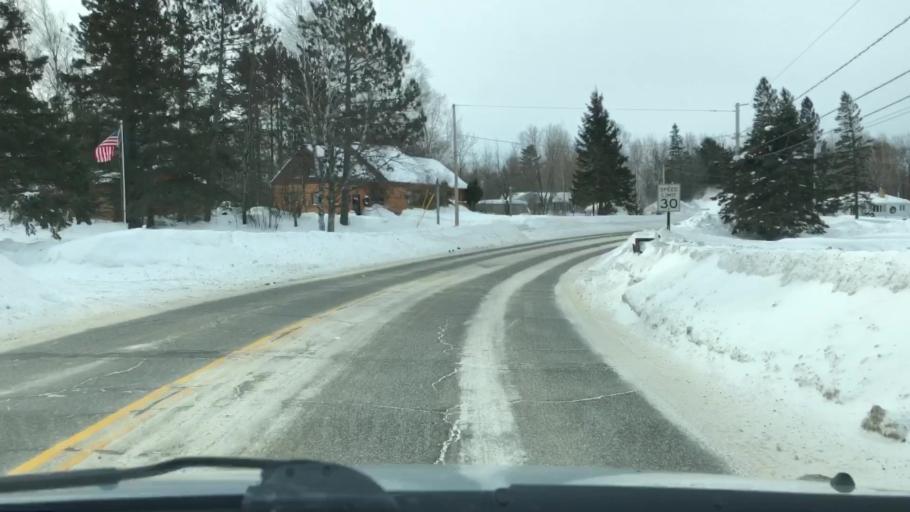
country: US
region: Minnesota
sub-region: Saint Louis County
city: Duluth
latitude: 46.7941
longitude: -92.1494
